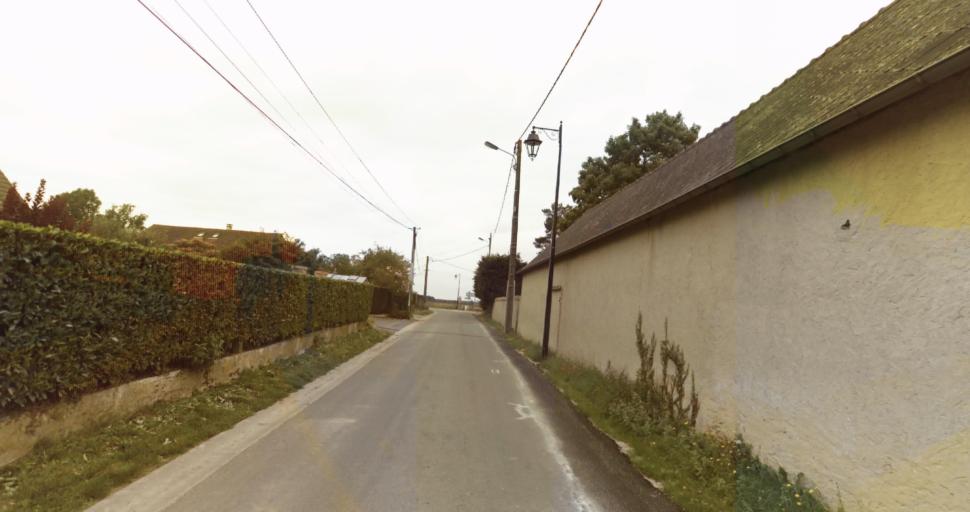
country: FR
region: Haute-Normandie
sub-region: Departement de l'Eure
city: Evreux
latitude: 48.9753
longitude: 1.2402
